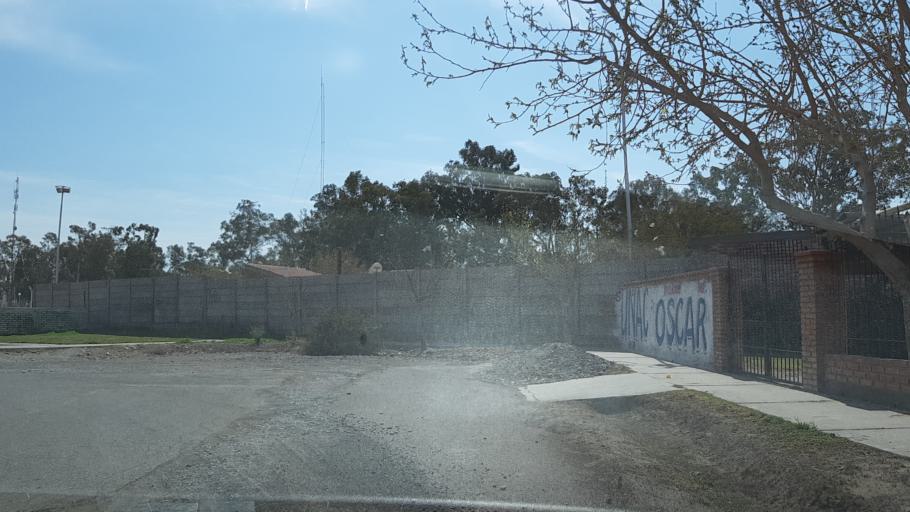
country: AR
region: San Juan
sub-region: Departamento de Zonda
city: Zonda
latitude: -31.5524
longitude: -68.7311
